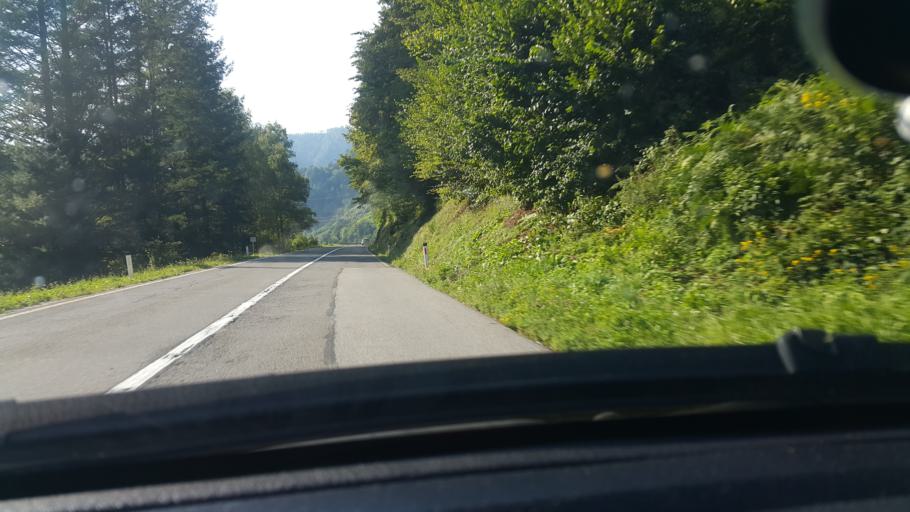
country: SI
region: Lovrenc na Pohorju
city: Lovrenc na Pohorju
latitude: 46.5768
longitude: 15.4076
